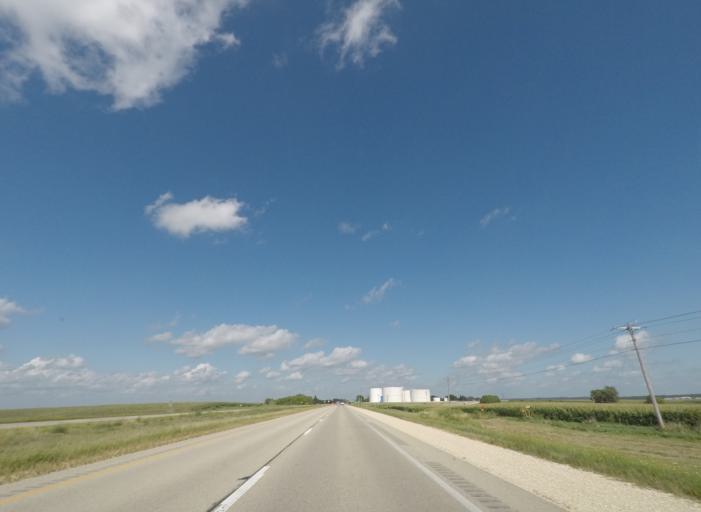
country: US
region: Iowa
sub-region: Dubuque County
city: Asbury
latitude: 42.4106
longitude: -90.7372
